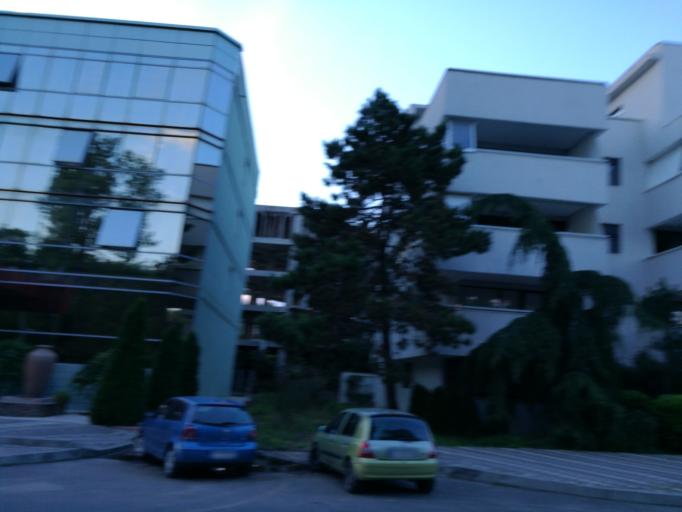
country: RO
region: Constanta
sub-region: Comuna Douazeci si Trei August
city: Douazeci si Trei August
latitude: 43.8732
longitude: 28.6014
